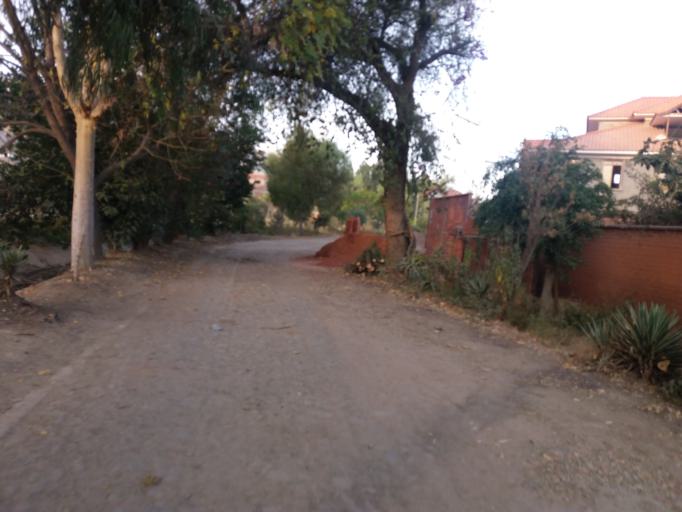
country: BO
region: Cochabamba
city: Cochabamba
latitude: -17.3567
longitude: -66.2003
